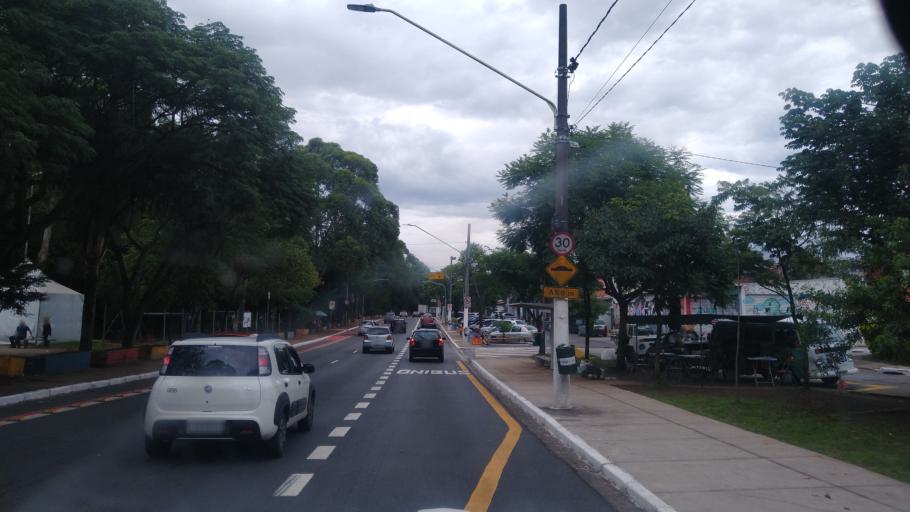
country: BR
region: Sao Paulo
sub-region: Guarulhos
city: Guarulhos
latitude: -23.5142
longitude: -46.5327
